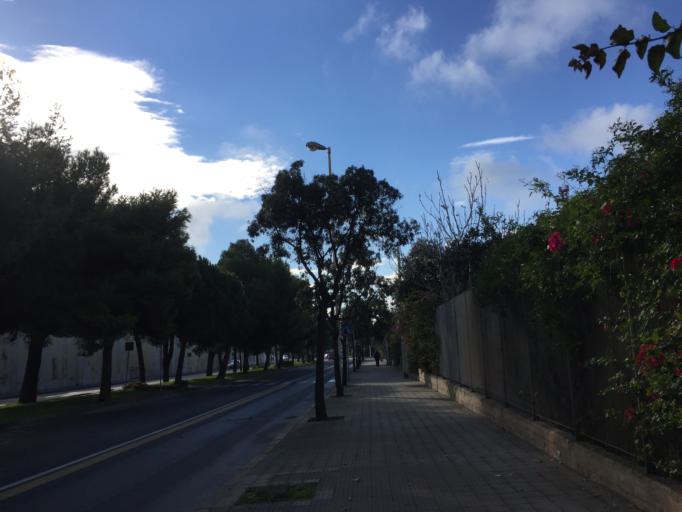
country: IT
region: Sardinia
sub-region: Provincia di Cagliari
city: Cagliari
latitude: 39.2116
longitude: 9.1230
